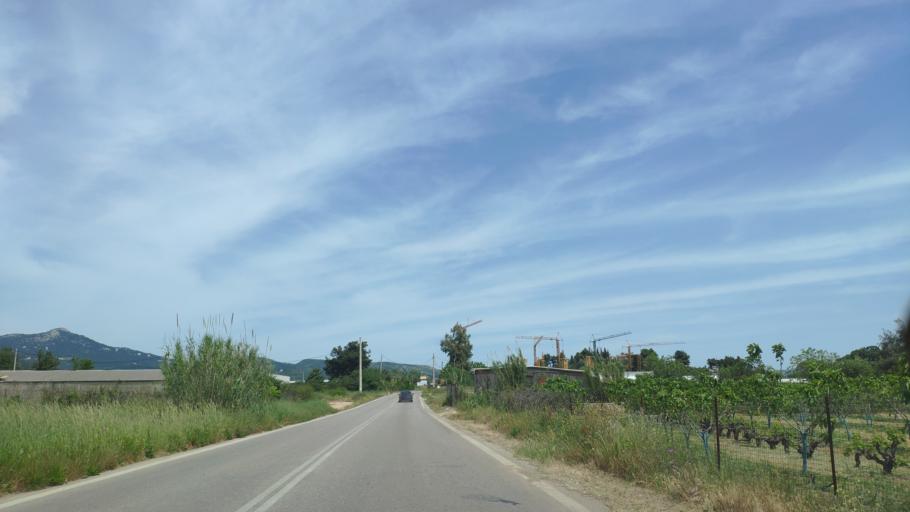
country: GR
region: Attica
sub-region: Nomarchia Anatolikis Attikis
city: Afidnes
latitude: 38.1802
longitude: 23.8571
